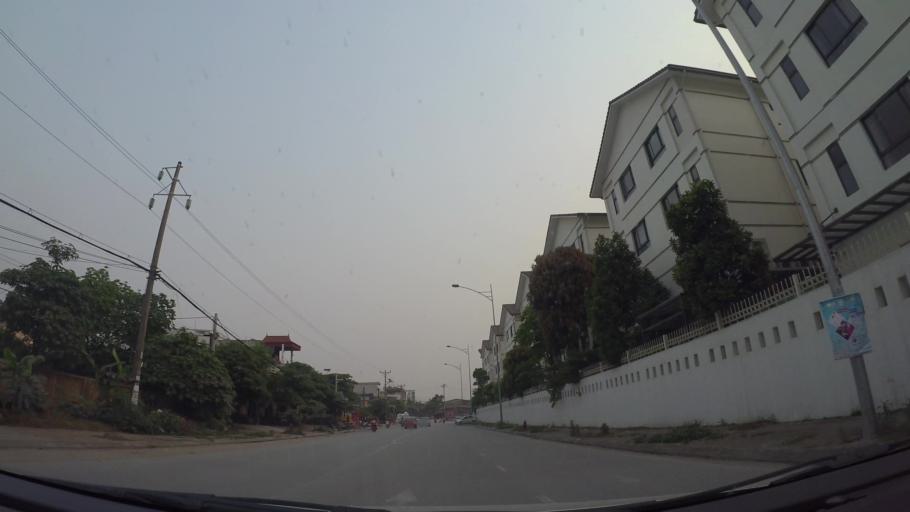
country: VN
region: Ha Noi
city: Cau Dien
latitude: 20.9980
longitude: 105.7246
